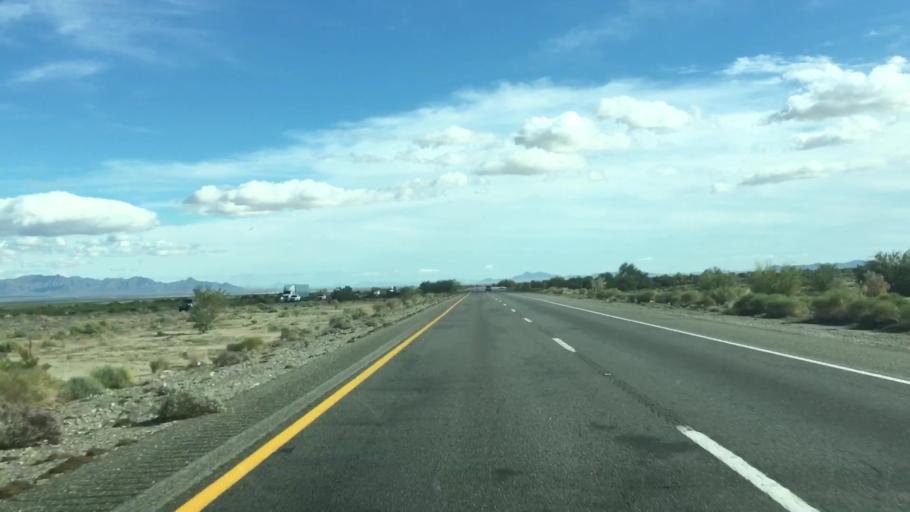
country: US
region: California
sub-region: Riverside County
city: Mesa Verde
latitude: 33.6601
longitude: -115.1679
